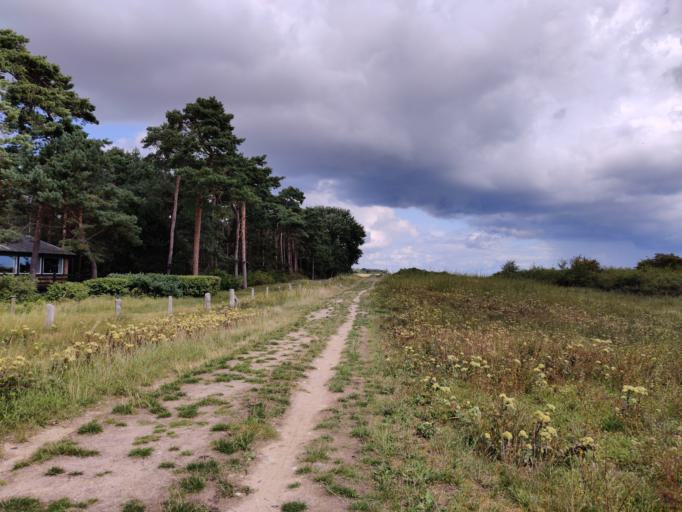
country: DK
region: Zealand
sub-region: Guldborgsund Kommune
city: Nykobing Falster
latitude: 54.7170
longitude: 12.0024
